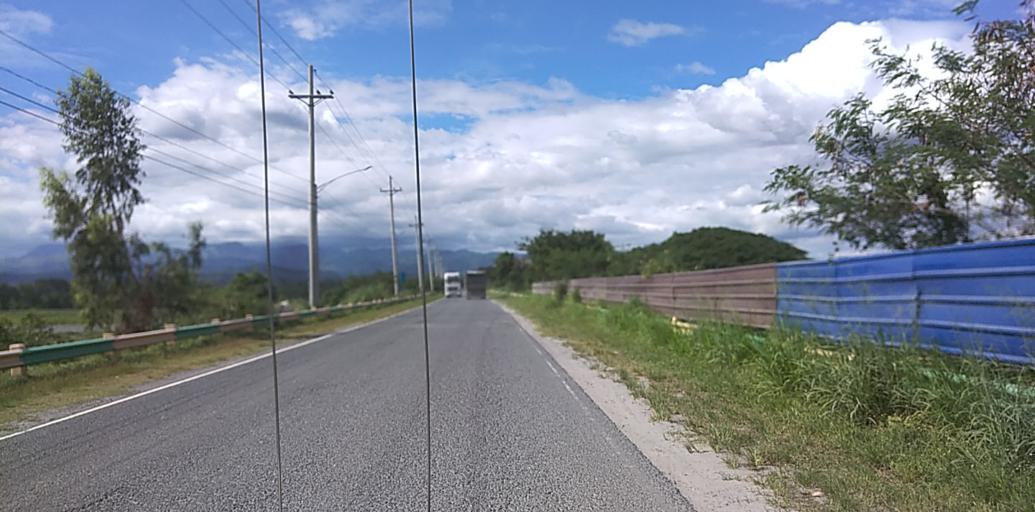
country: PH
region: Central Luzon
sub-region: Province of Pampanga
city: Porac
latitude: 15.0834
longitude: 120.5464
